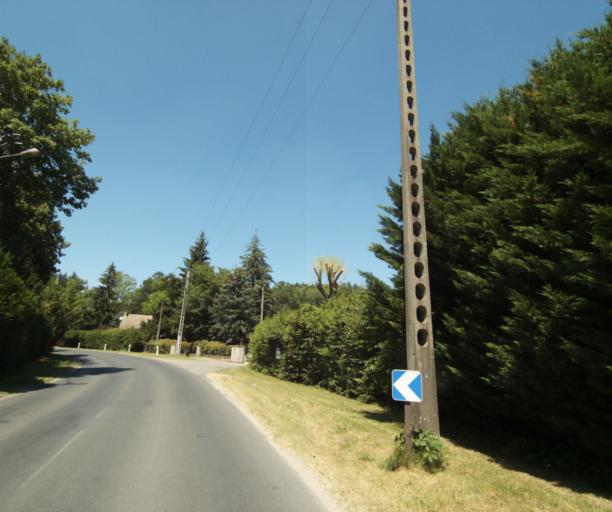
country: FR
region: Ile-de-France
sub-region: Departement de Seine-et-Marne
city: Noisy-sur-Ecole
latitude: 48.3623
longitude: 2.5205
